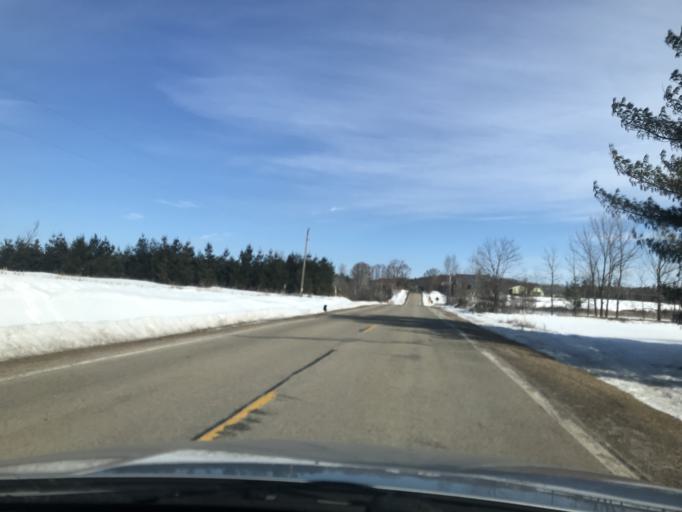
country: US
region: Wisconsin
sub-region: Oconto County
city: Gillett
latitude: 44.9569
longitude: -88.2651
